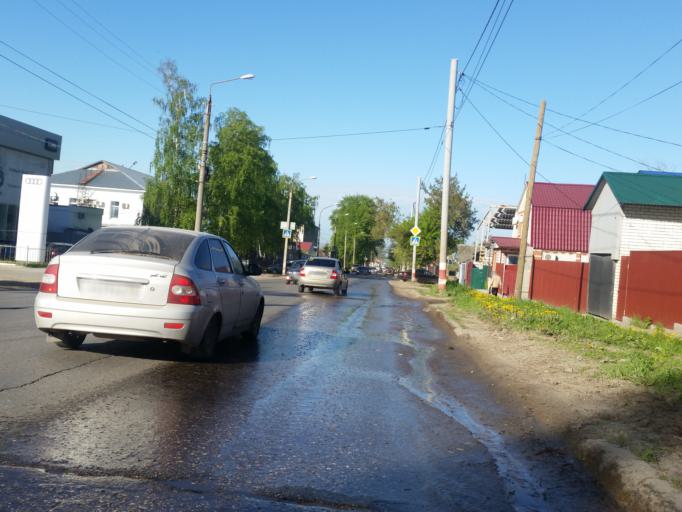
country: RU
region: Ulyanovsk
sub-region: Ulyanovskiy Rayon
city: Ulyanovsk
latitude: 54.3363
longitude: 48.3795
